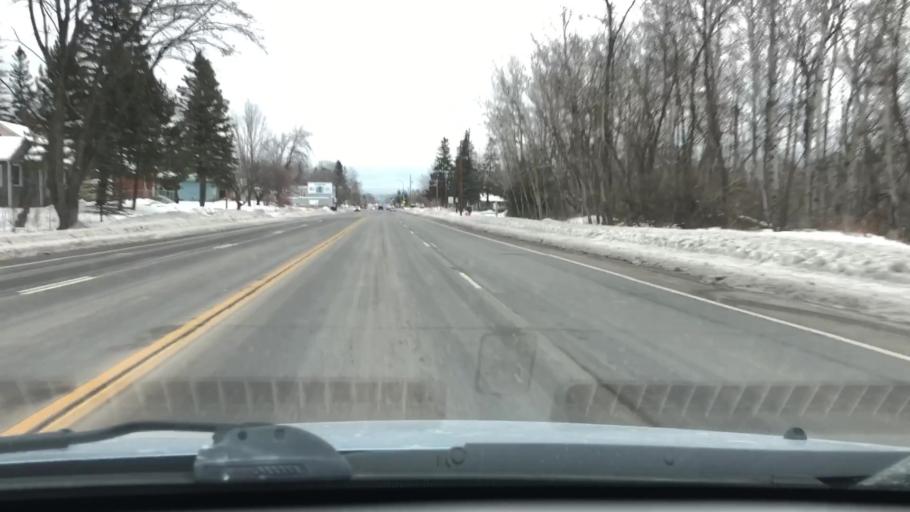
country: US
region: Minnesota
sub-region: Saint Louis County
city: Proctor
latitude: 46.7197
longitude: -92.1965
